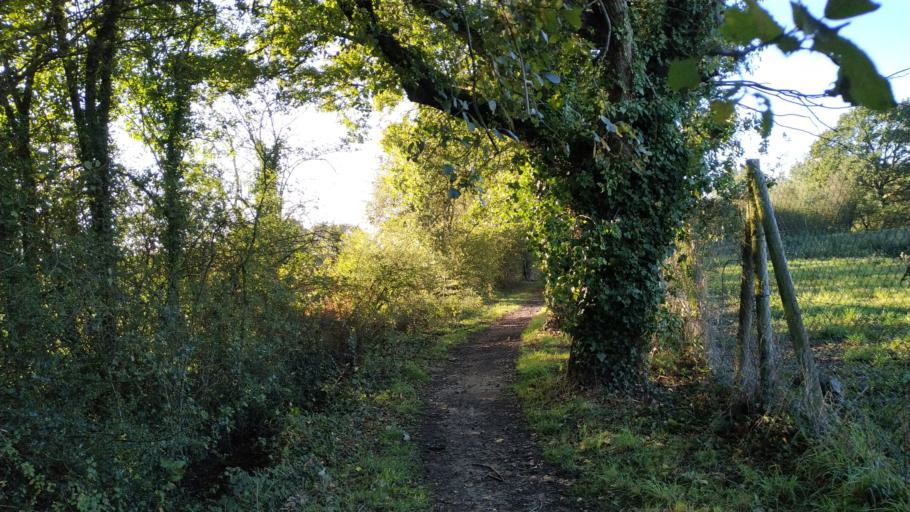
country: FR
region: Brittany
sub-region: Departement d'Ille-et-Vilaine
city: Chantepie
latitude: 48.0797
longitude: -1.6239
